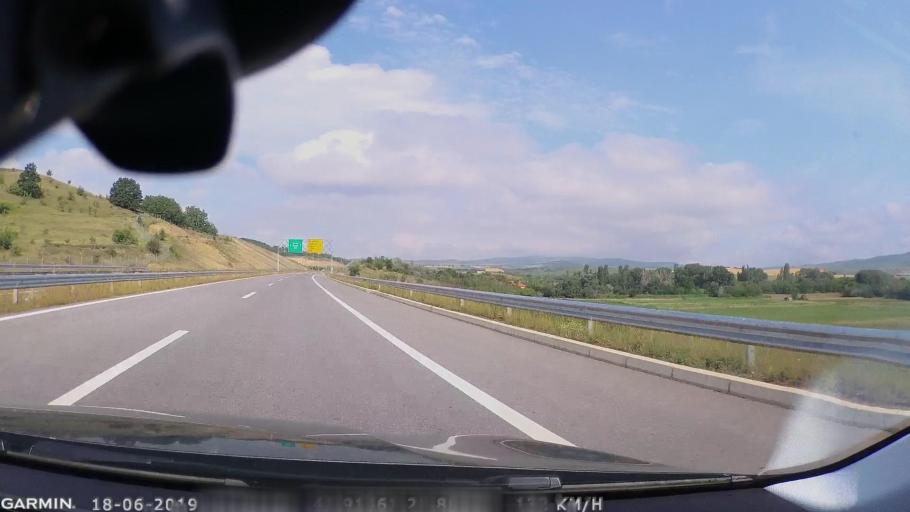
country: MK
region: Sveti Nikole
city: Gorobinci
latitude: 41.9137
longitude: 21.8904
